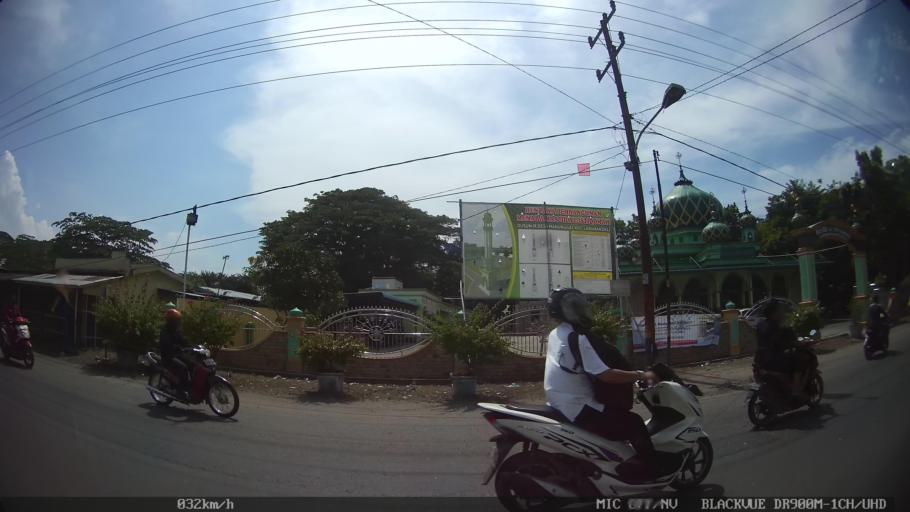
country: ID
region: North Sumatra
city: Medan
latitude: 3.6541
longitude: 98.6569
